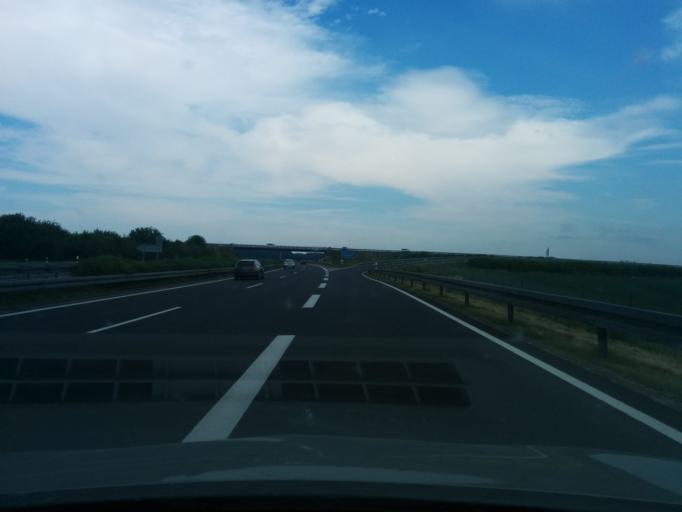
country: DE
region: Mecklenburg-Vorpommern
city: Jarmen
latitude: 53.9461
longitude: 13.3666
